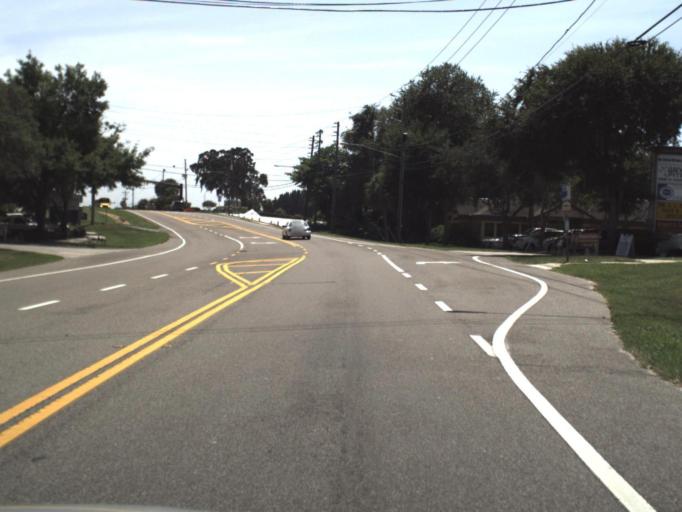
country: US
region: Florida
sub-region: Pinellas County
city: Tarpon Springs
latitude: 28.1349
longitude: -82.7581
